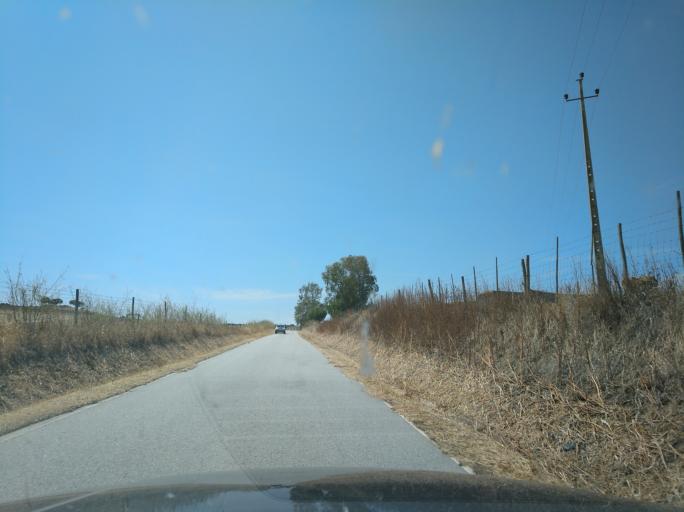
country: PT
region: Portalegre
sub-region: Campo Maior
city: Campo Maior
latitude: 38.9625
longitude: -7.1133
